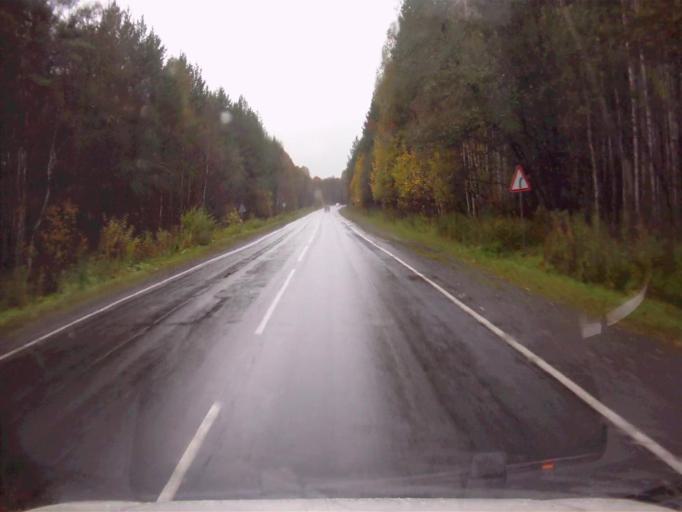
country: RU
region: Chelyabinsk
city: Verkhniy Ufaley
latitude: 55.9703
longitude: 60.3625
